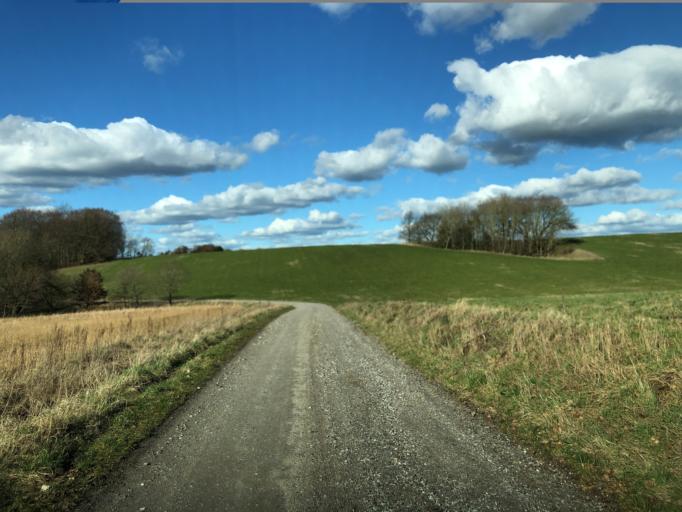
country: DK
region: Central Jutland
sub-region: Favrskov Kommune
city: Hammel
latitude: 56.3052
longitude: 9.9182
